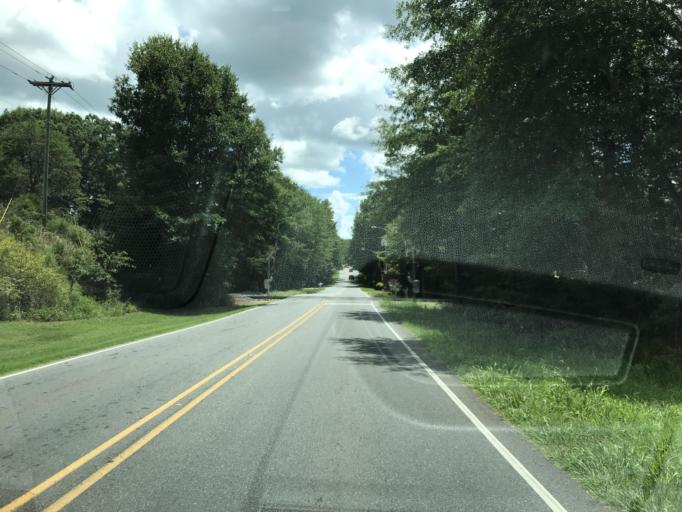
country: US
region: North Carolina
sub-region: Cleveland County
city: Shelby
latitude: 35.3055
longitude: -81.5163
